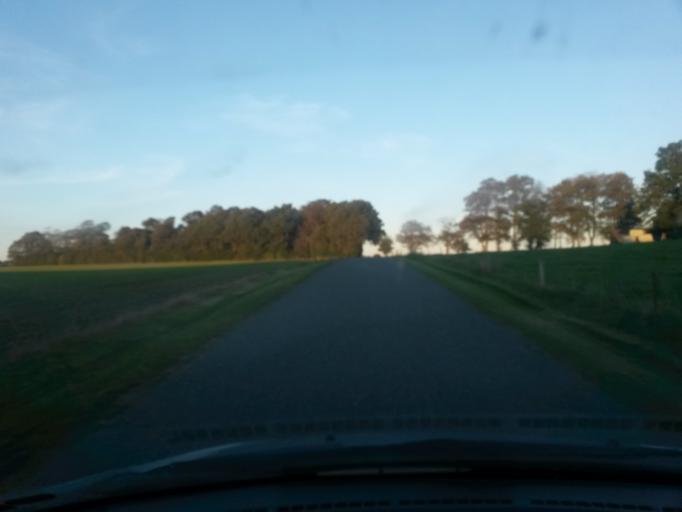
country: DK
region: Central Jutland
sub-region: Silkeborg Kommune
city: Kjellerup
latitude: 56.2943
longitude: 9.3657
